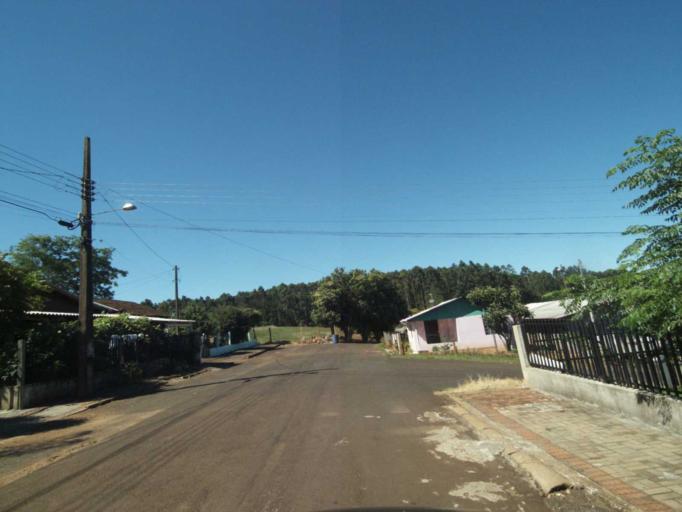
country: BR
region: Parana
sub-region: Coronel Vivida
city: Coronel Vivida
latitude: -25.9573
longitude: -52.8094
